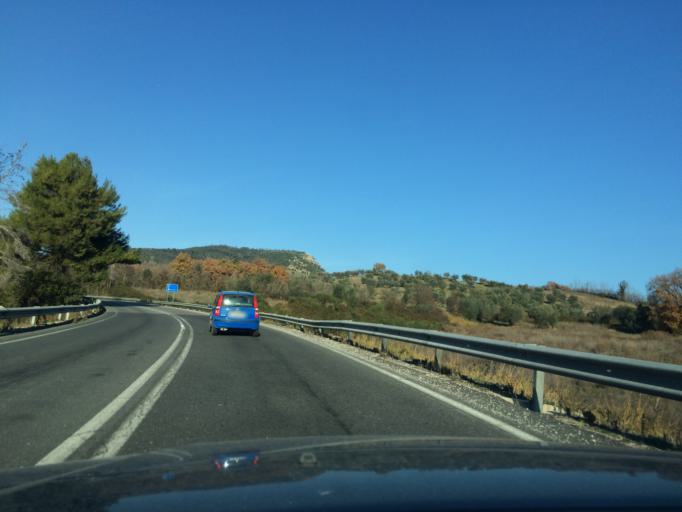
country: IT
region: Umbria
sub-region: Provincia di Terni
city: Fornole
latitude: 42.5325
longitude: 12.4751
